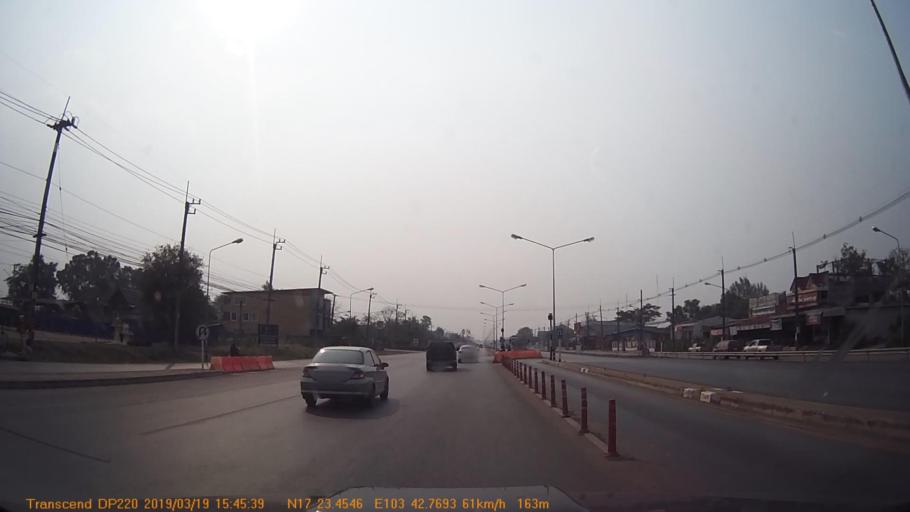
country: TH
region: Sakon Nakhon
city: Phang Khon
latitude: 17.3909
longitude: 103.7127
